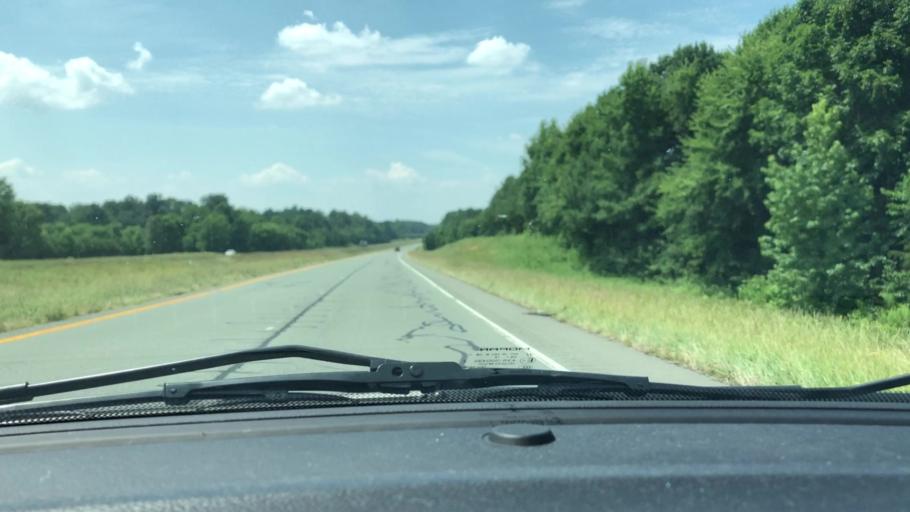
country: US
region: North Carolina
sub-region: Randolph County
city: Liberty
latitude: 35.7913
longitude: -79.5272
